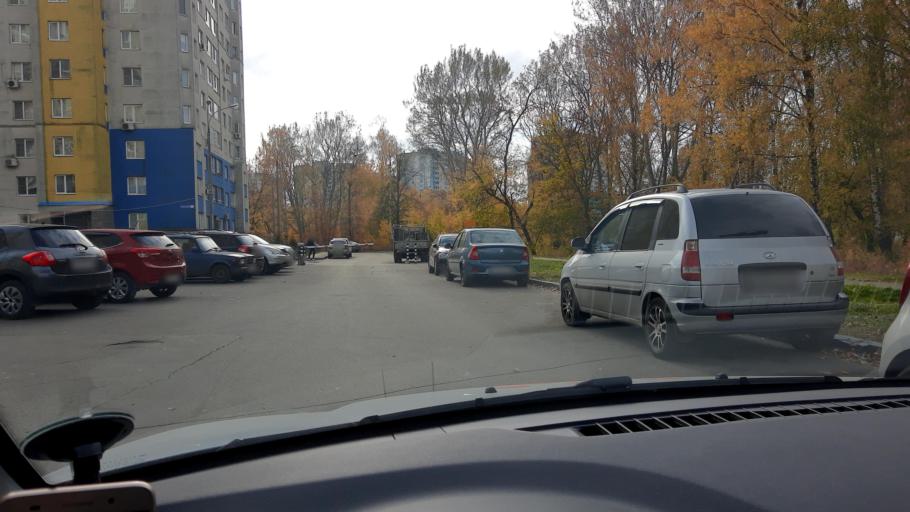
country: RU
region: Nizjnij Novgorod
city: Gorbatovka
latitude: 56.2417
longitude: 43.8456
